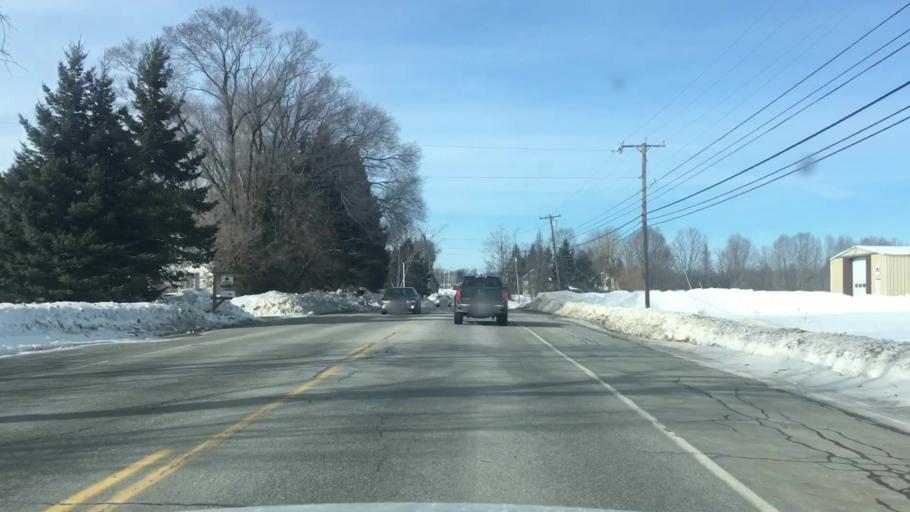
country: US
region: Maine
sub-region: Penobscot County
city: Charleston
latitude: 45.0132
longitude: -69.0269
